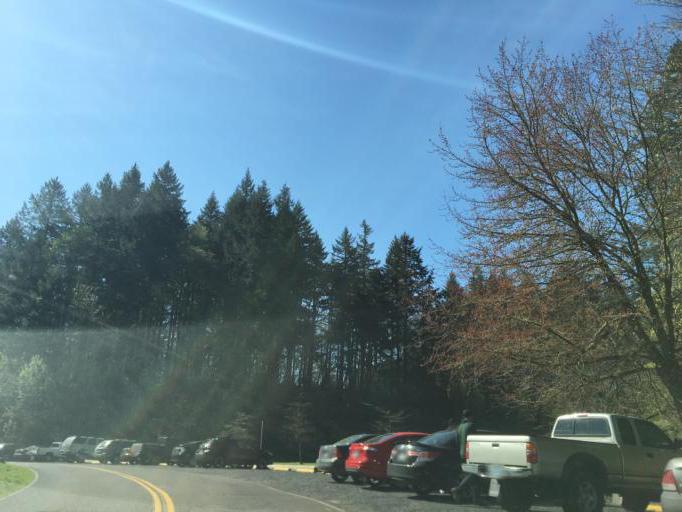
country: US
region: Oregon
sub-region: Multnomah County
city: Portland
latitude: 45.5149
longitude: -122.7100
